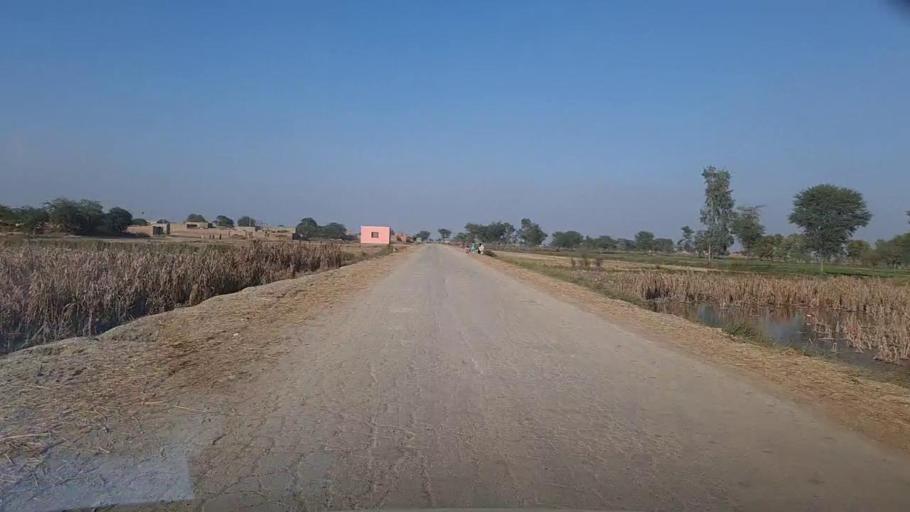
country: PK
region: Sindh
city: Phulji
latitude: 26.8580
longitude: 67.7941
